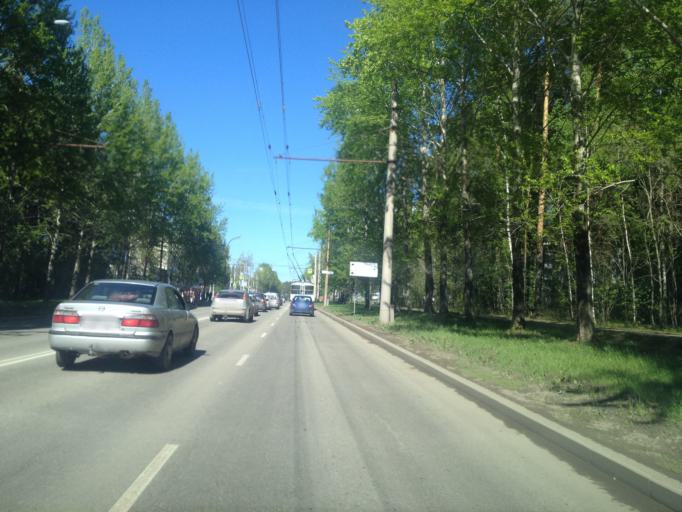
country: RU
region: Sverdlovsk
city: Sovkhoznyy
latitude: 56.7753
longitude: 60.5501
